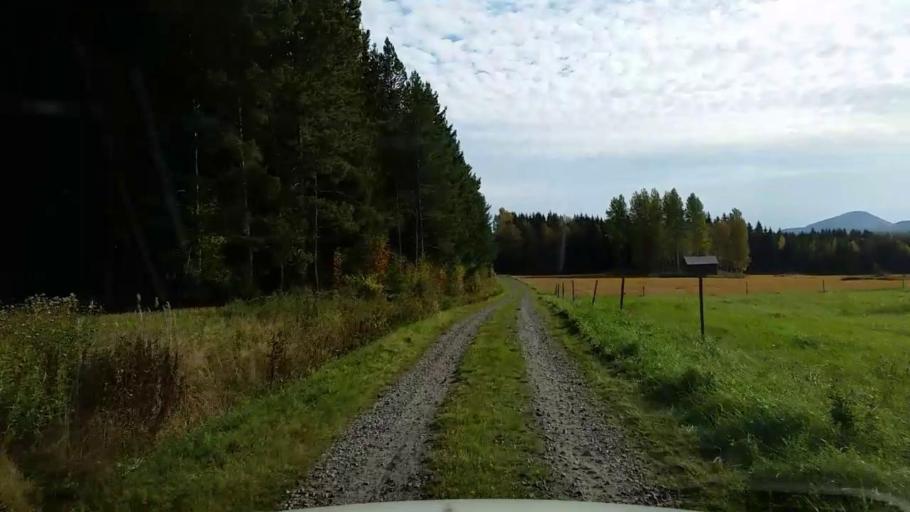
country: SE
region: Gaevleborg
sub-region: Ljusdals Kommun
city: Jaervsoe
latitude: 61.7824
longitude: 16.1707
